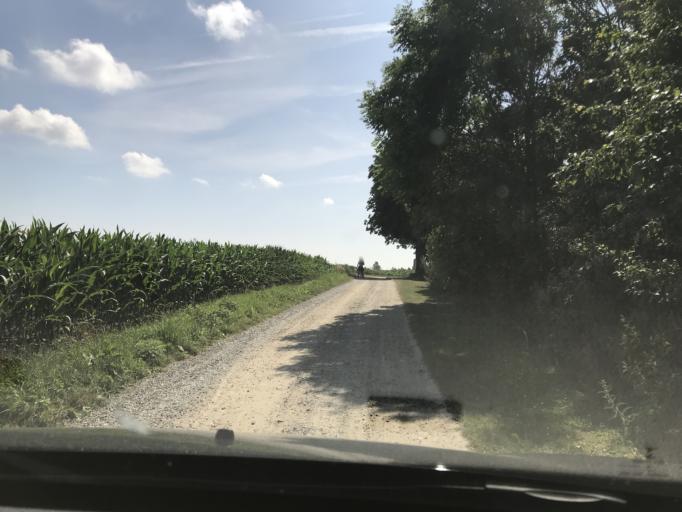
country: DK
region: South Denmark
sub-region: AEro Kommune
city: AEroskobing
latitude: 54.9068
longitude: 10.3211
